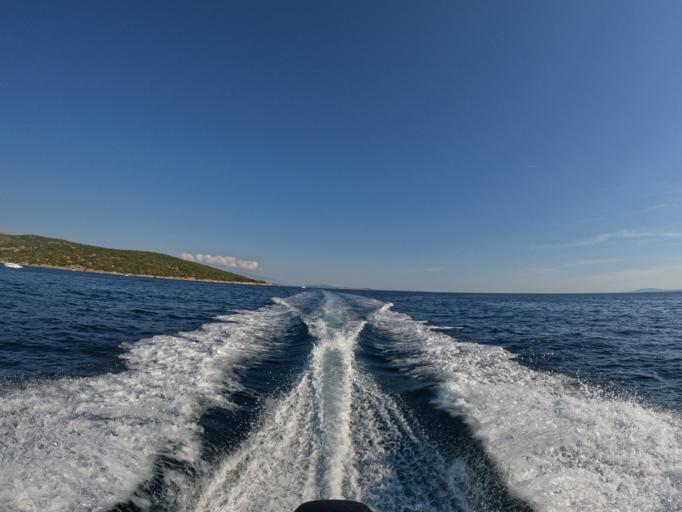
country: HR
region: Primorsko-Goranska
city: Punat
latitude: 44.9872
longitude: 14.6081
